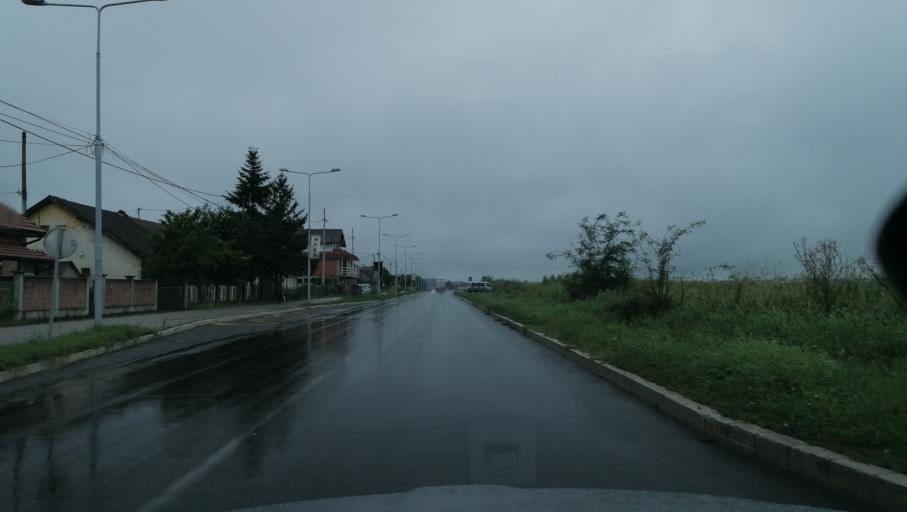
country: RS
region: Central Serbia
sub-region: Raski Okrug
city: Kraljevo
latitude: 43.7294
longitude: 20.6713
